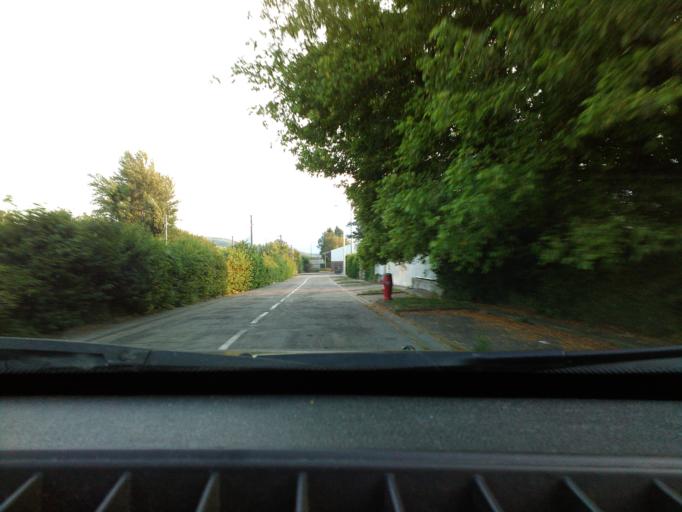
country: FR
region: Rhone-Alpes
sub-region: Departement de l'Isere
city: Eybens
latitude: 45.1592
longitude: 5.7495
